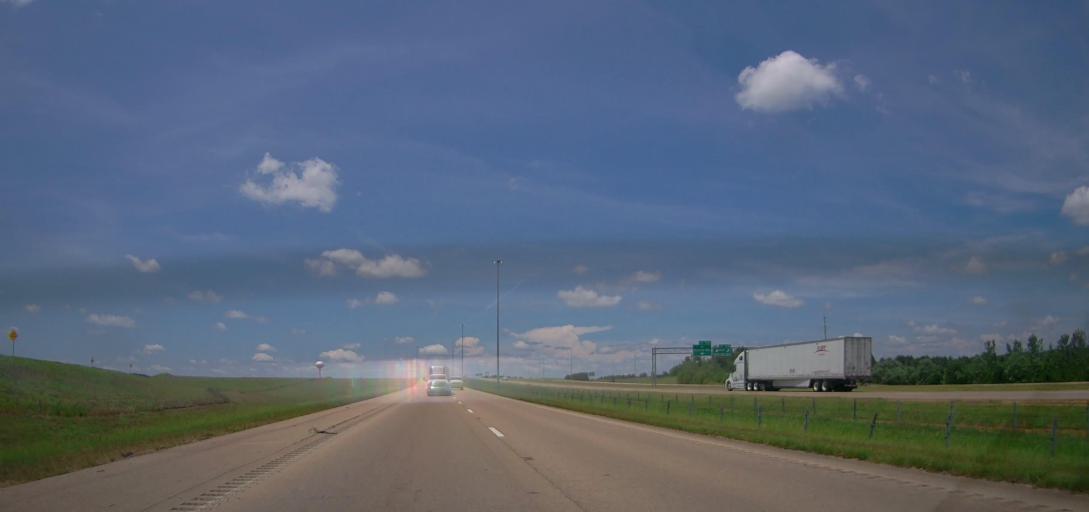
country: US
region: Mississippi
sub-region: Union County
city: New Albany
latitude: 34.3818
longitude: -88.8848
